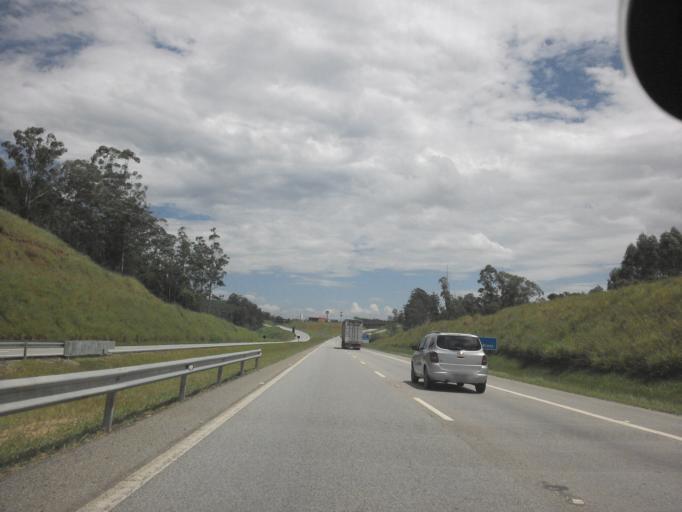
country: BR
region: Sao Paulo
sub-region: Cacapava
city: Cacapava
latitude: -23.0967
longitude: -45.6224
